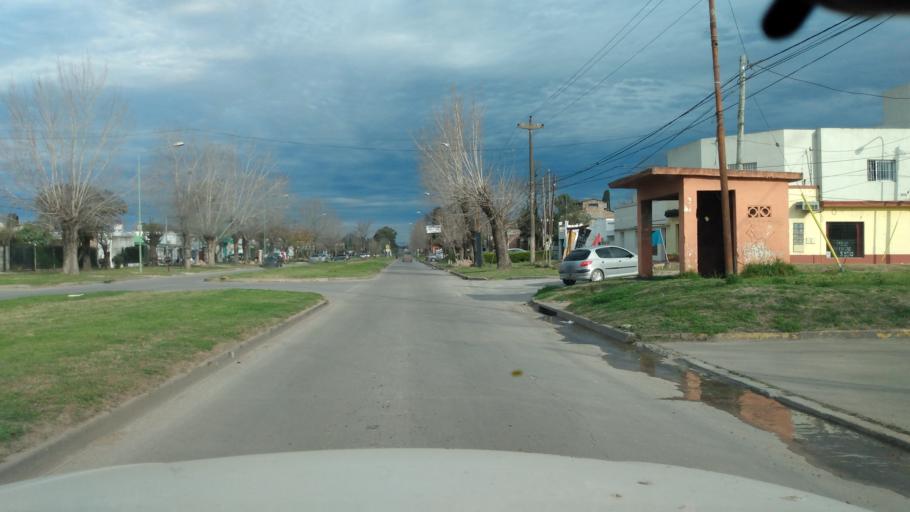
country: AR
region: Buenos Aires
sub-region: Partido de Lujan
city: Lujan
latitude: -34.5661
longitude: -59.1347
